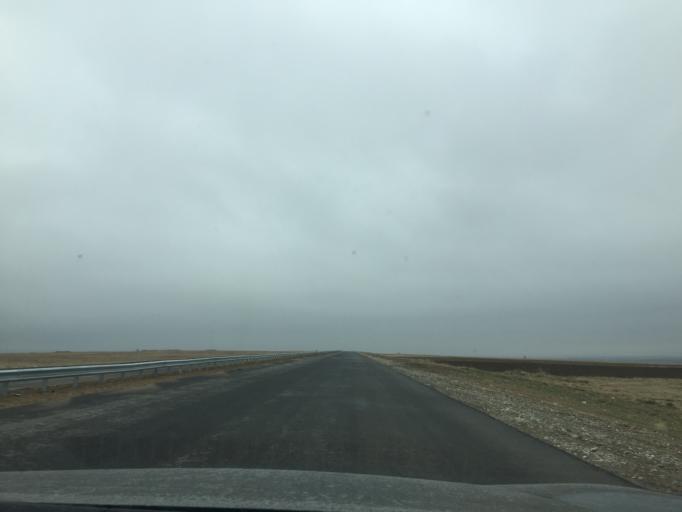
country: KZ
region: Ongtustik Qazaqstan
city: Kokterek
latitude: 42.5434
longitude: 70.2774
